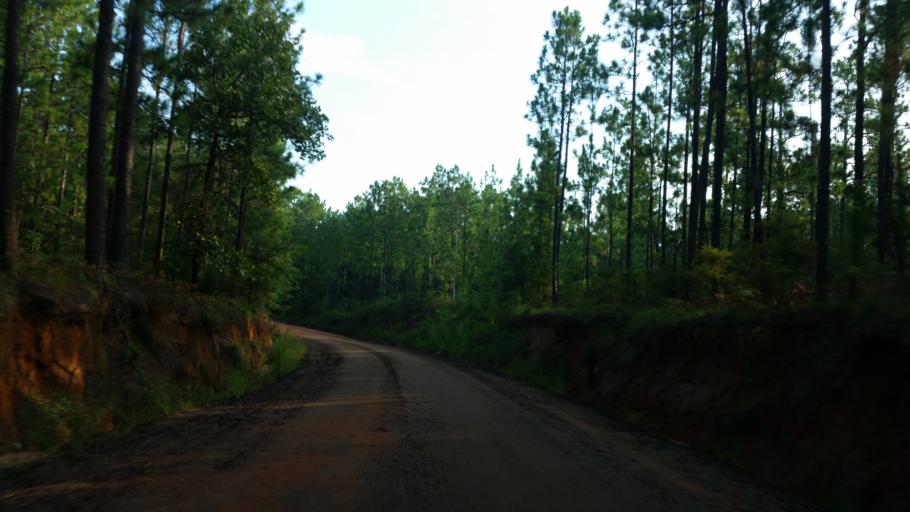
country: US
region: Alabama
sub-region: Escambia County
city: Atmore
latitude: 30.9541
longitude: -87.5719
